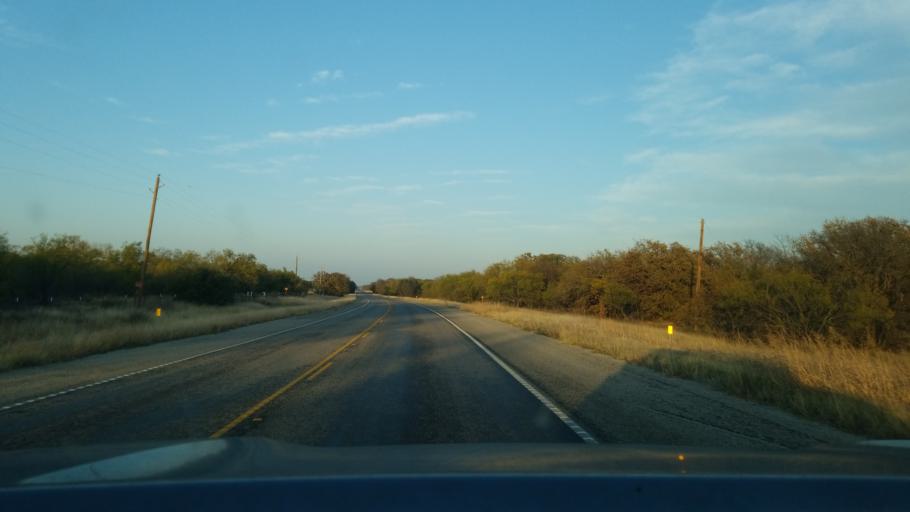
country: US
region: Texas
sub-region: Eastland County
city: Cisco
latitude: 32.4104
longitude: -98.9473
